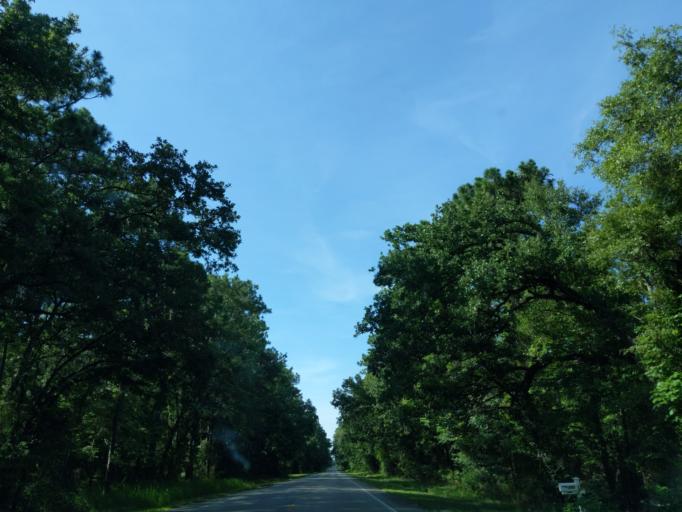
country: US
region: Florida
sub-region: Leon County
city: Woodville
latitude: 30.2989
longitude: -84.3121
